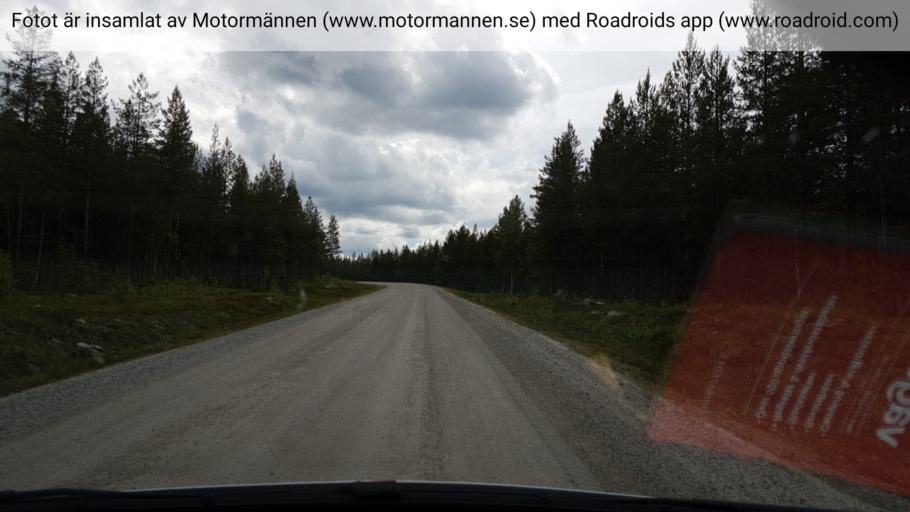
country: SE
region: Vaesternorrland
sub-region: Solleftea Kommun
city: Solleftea
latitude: 63.3777
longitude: 17.4829
